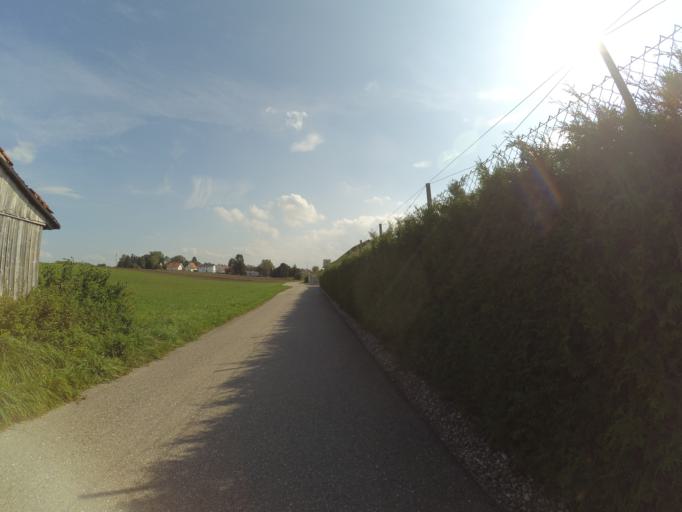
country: DE
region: Bavaria
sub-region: Swabia
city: Buchloe
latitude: 48.0473
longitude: 10.7267
